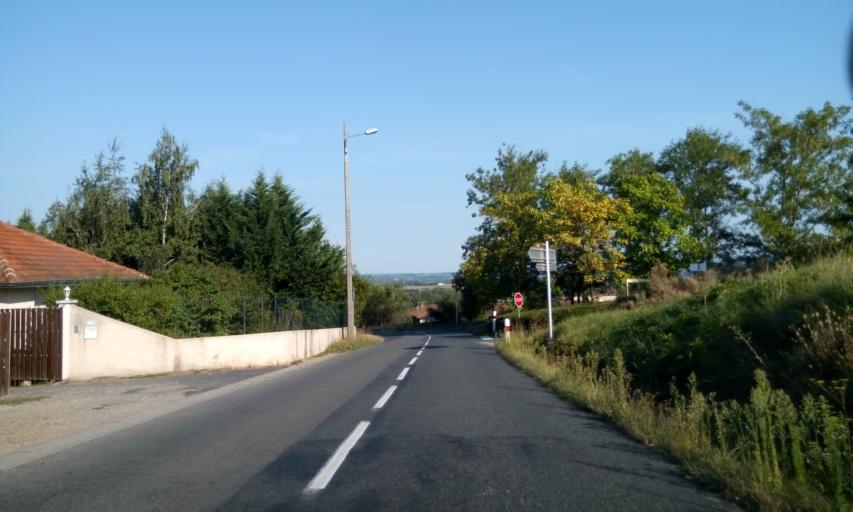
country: FR
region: Rhone-Alpes
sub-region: Departement du Rhone
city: Anse
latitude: 45.9287
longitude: 4.7033
